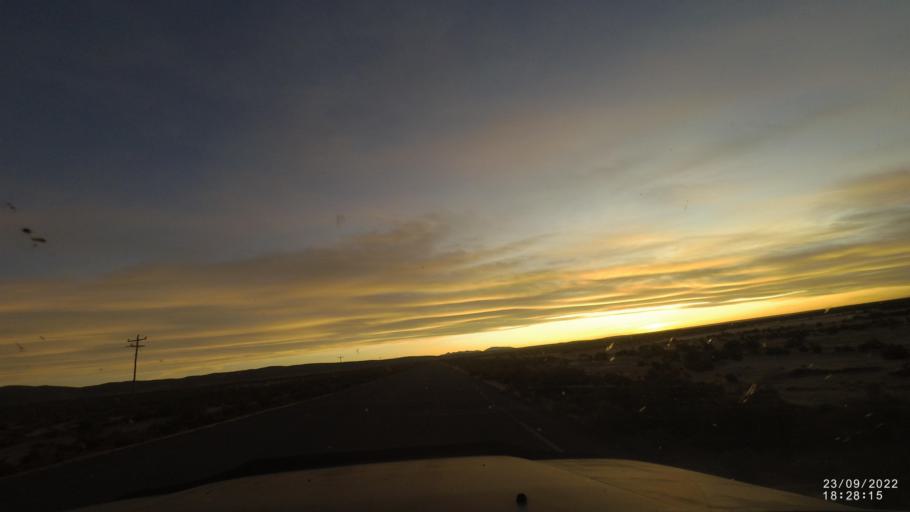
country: BO
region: Oruro
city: Challapata
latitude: -19.3360
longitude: -67.1745
